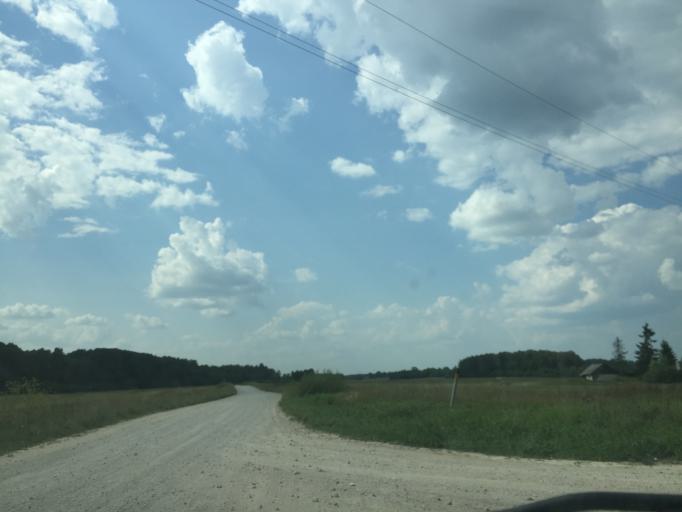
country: LV
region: Auces Novads
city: Auce
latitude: 56.4014
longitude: 23.0582
